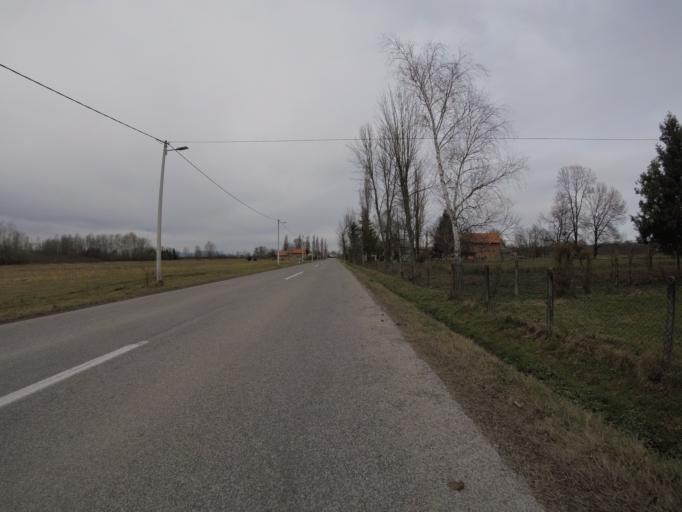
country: HR
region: Grad Zagreb
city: Horvati
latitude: 45.5700
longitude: 15.8630
